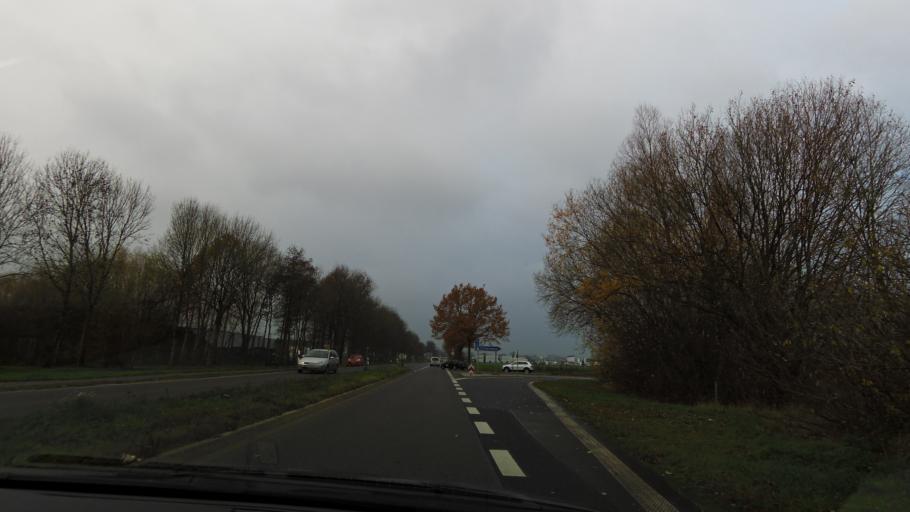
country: DE
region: North Rhine-Westphalia
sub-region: Regierungsbezirk Koln
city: Wassenberg
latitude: 51.0446
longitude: 6.1664
